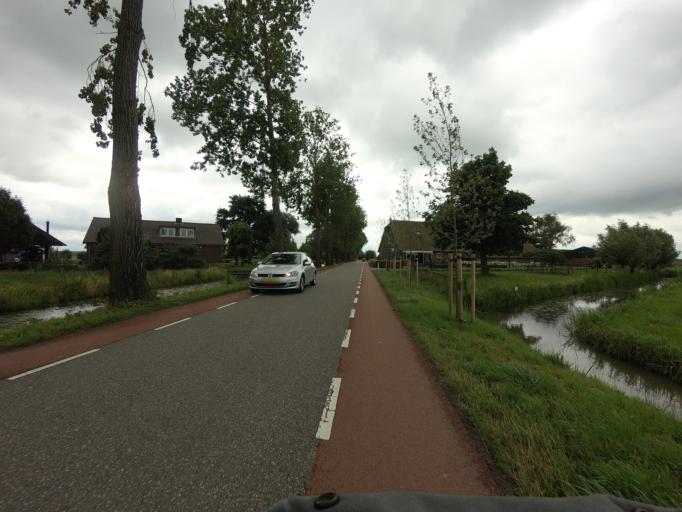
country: NL
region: Utrecht
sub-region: Gemeente IJsselstein
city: IJsselstein
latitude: 52.0508
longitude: 5.0339
